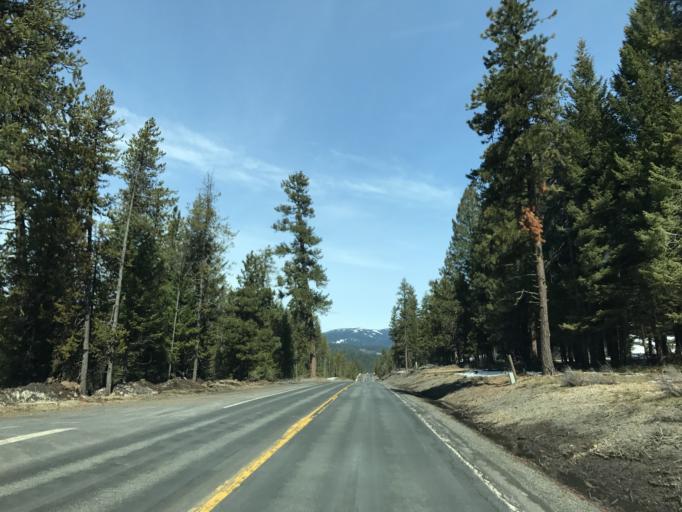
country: US
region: Idaho
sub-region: Valley County
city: McCall
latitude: 44.9409
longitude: -116.1667
